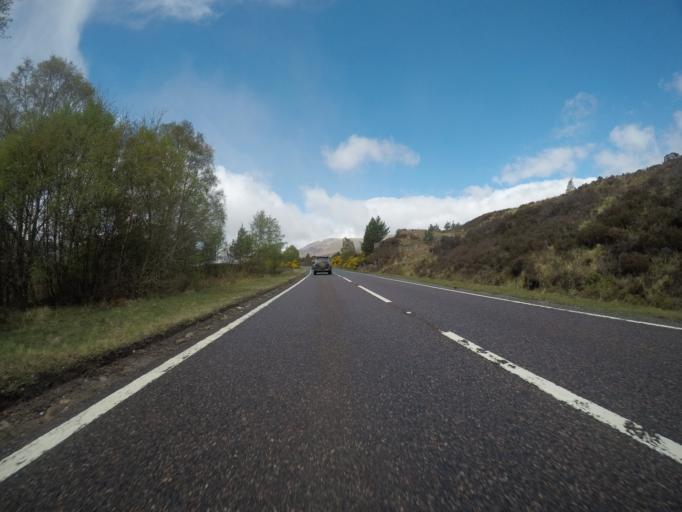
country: GB
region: Scotland
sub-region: Highland
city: Spean Bridge
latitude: 57.1462
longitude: -4.9969
